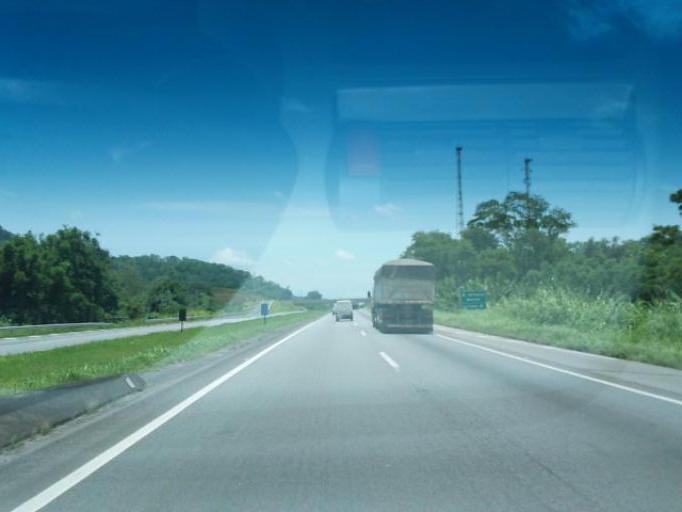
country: BR
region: Sao Paulo
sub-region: Miracatu
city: Miracatu
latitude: -24.3212
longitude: -47.5365
